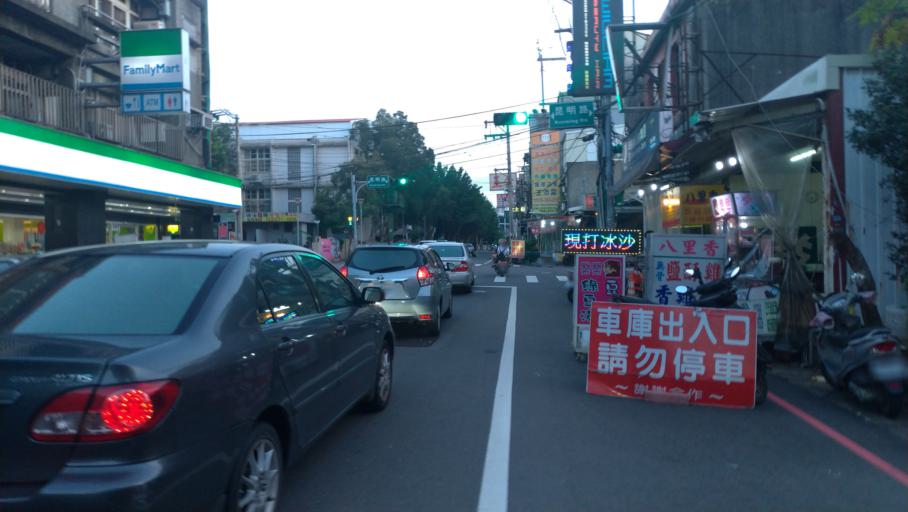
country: TW
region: Taiwan
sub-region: Taoyuan
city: Taoyuan
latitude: 24.9839
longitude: 121.3146
